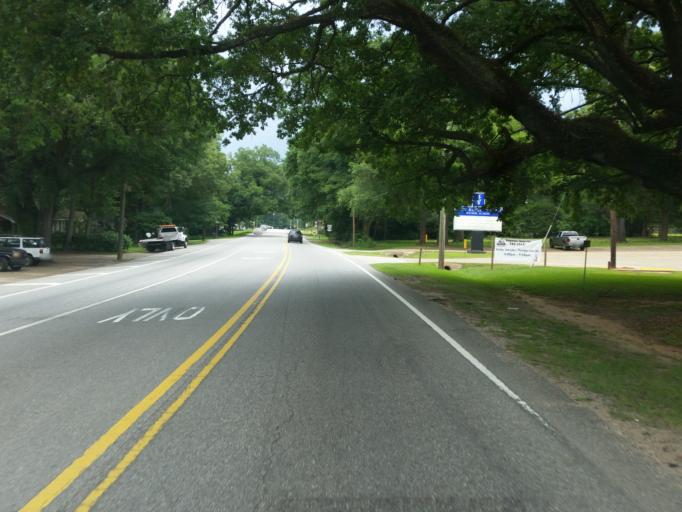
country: US
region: Mississippi
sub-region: Jackson County
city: Hurley
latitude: 30.8233
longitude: -88.3612
